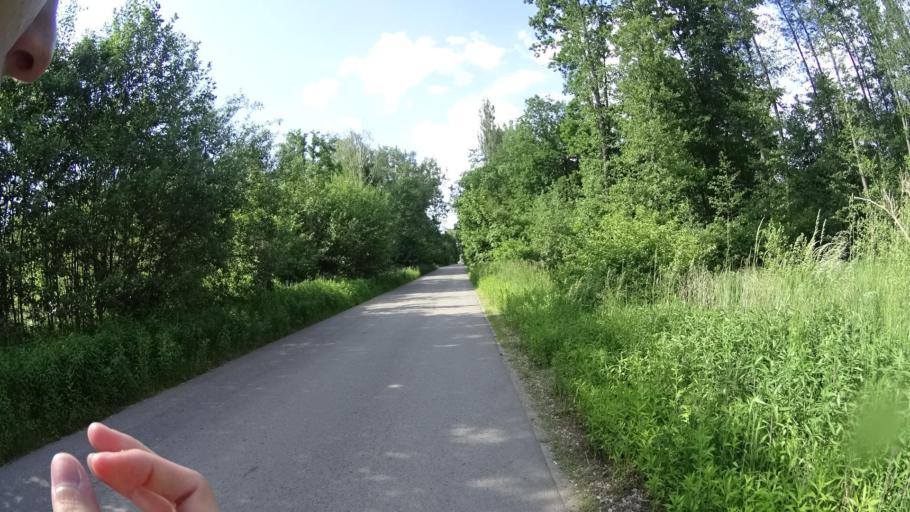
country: PL
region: Masovian Voivodeship
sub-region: Powiat pruszkowski
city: Nadarzyn
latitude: 52.0722
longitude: 20.8189
